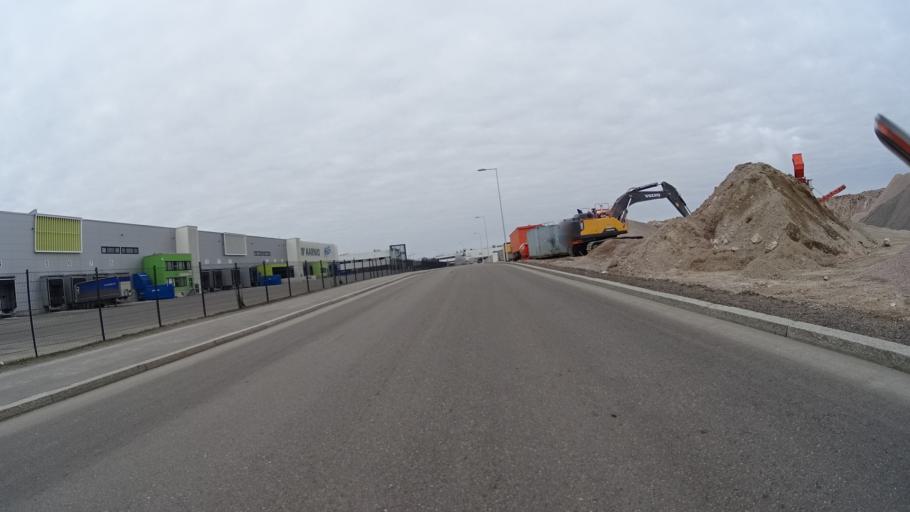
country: FI
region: Uusimaa
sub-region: Helsinki
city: Teekkarikylae
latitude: 60.3053
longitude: 24.8952
